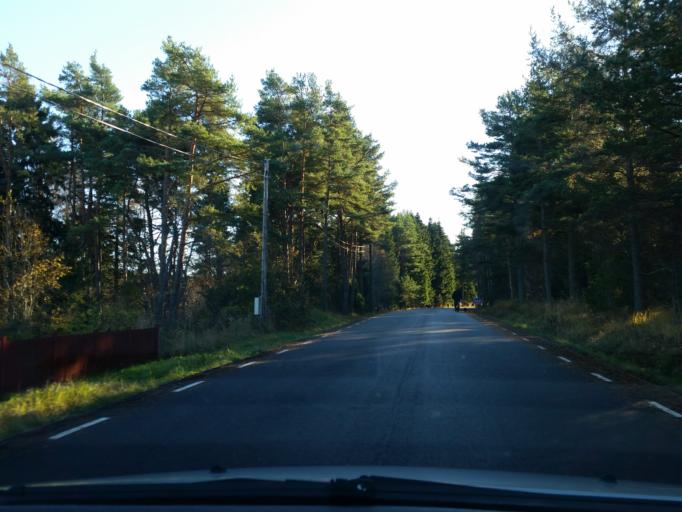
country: AX
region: Alands landsbygd
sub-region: Jomala
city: Jomala
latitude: 60.2003
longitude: 19.9576
